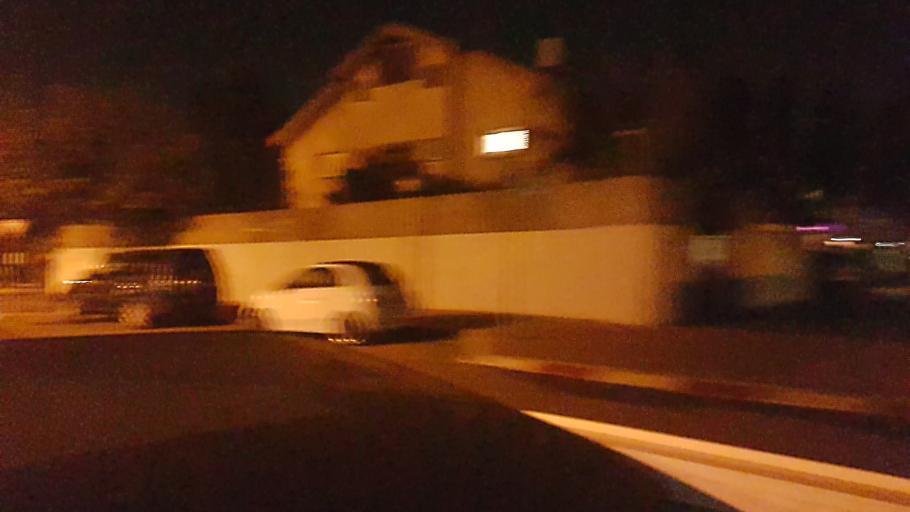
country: IL
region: Central District
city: Hod HaSharon
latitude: 32.1623
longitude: 34.8868
